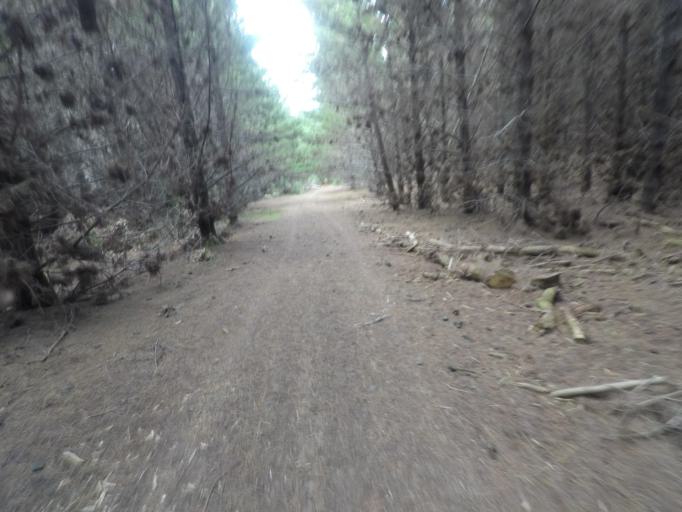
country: NZ
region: Auckland
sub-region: Auckland
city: Parakai
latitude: -36.6026
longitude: 174.2730
